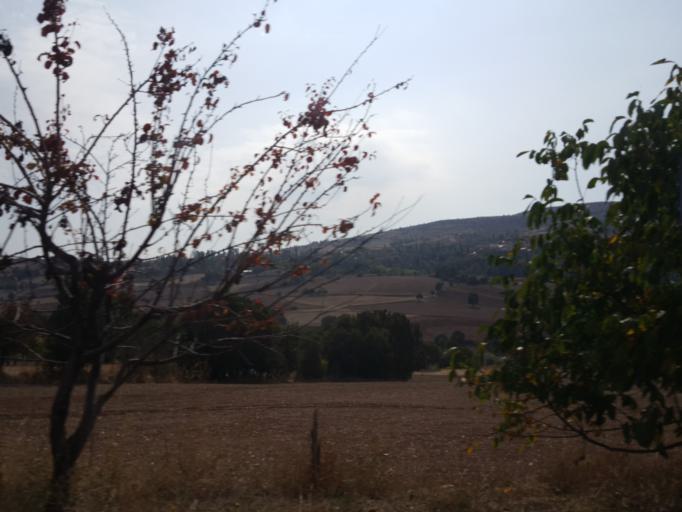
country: TR
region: Tokat
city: Zile
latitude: 40.3714
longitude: 35.8634
